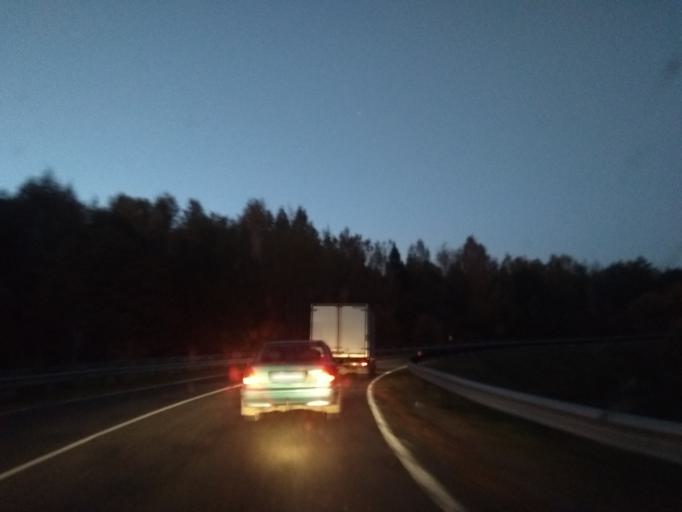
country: BY
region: Minsk
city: Enyerhyetykaw
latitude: 53.5901
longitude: 27.0375
